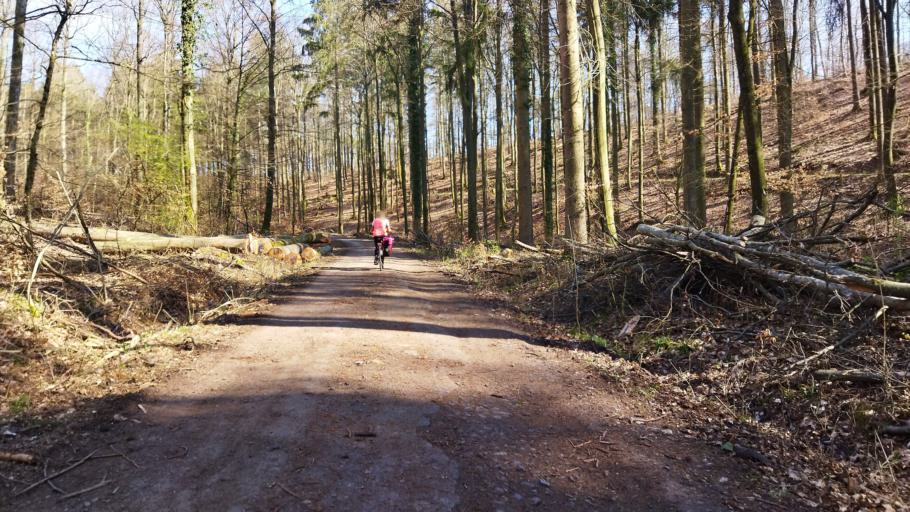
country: DE
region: Baden-Wuerttemberg
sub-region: Regierungsbezirk Stuttgart
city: Zaberfeld
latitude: 49.0279
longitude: 8.9250
